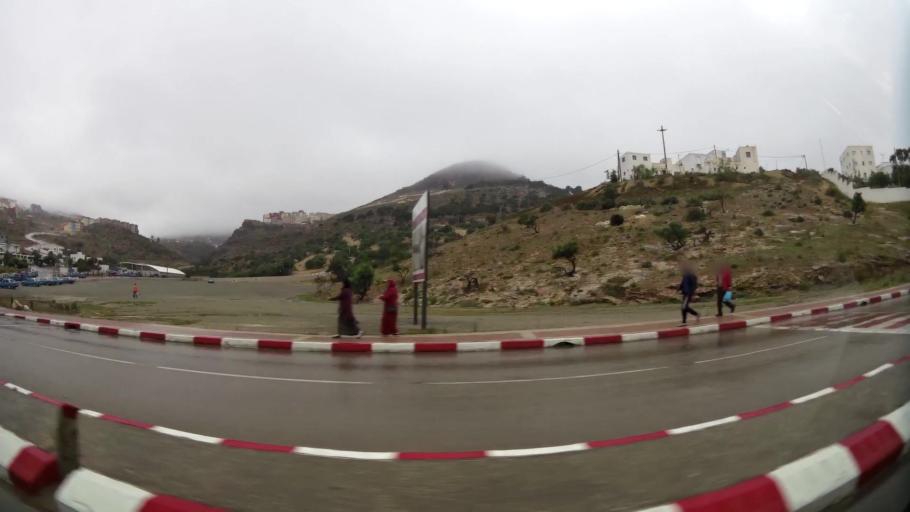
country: MA
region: Taza-Al Hoceima-Taounate
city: Al Hoceima
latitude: 35.2343
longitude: -3.9275
